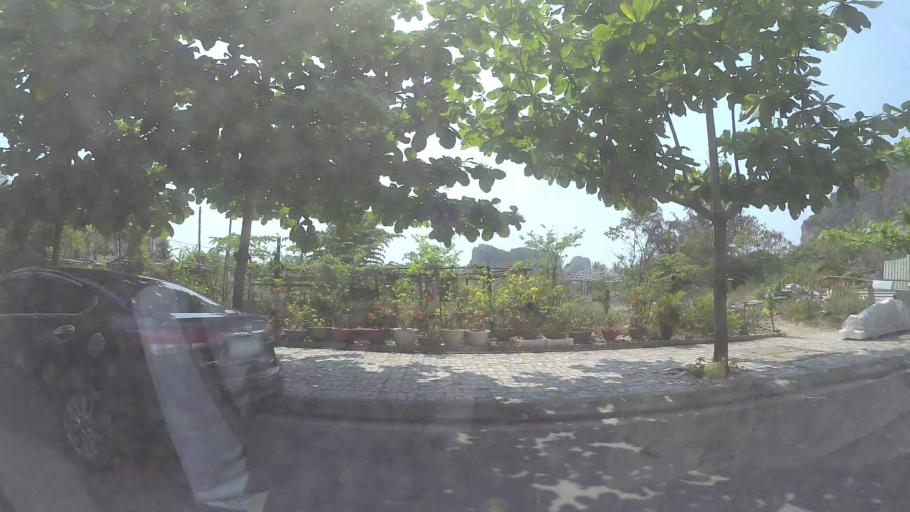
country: VN
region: Da Nang
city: Ngu Hanh Son
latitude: 16.0019
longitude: 108.2664
